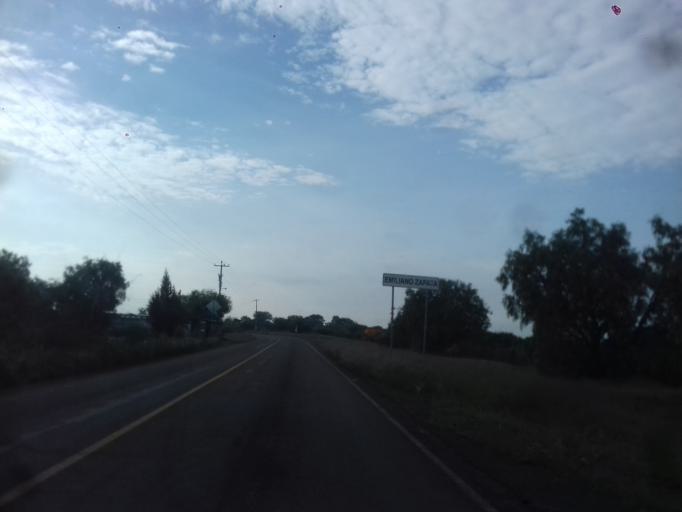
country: MX
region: Aguascalientes
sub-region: Aguascalientes
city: San Sebastian [Fraccionamiento]
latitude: 21.7952
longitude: -102.2399
